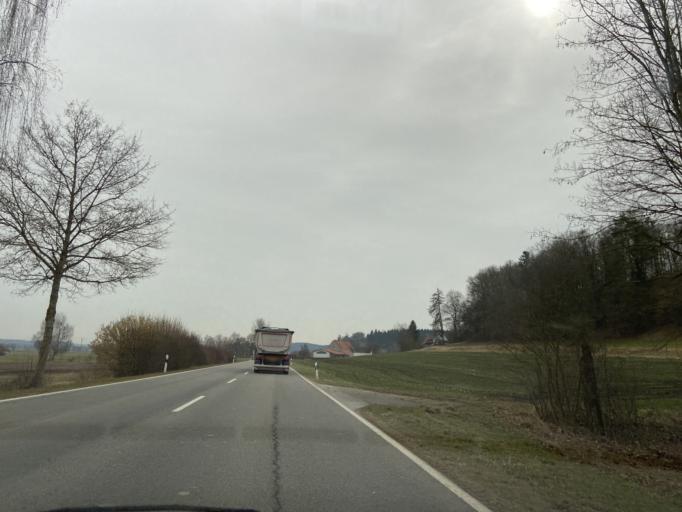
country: DE
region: Baden-Wuerttemberg
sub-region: Tuebingen Region
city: Ostrach
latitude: 47.9855
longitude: 9.3381
